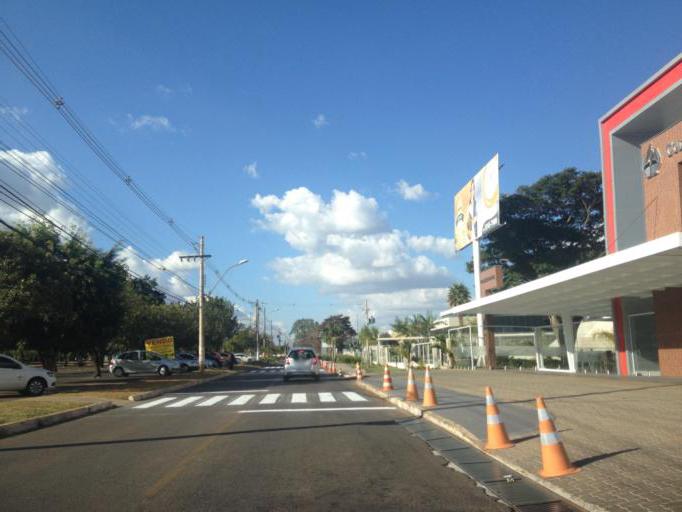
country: BR
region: Federal District
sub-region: Brasilia
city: Brasilia
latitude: -15.8292
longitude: -47.9053
